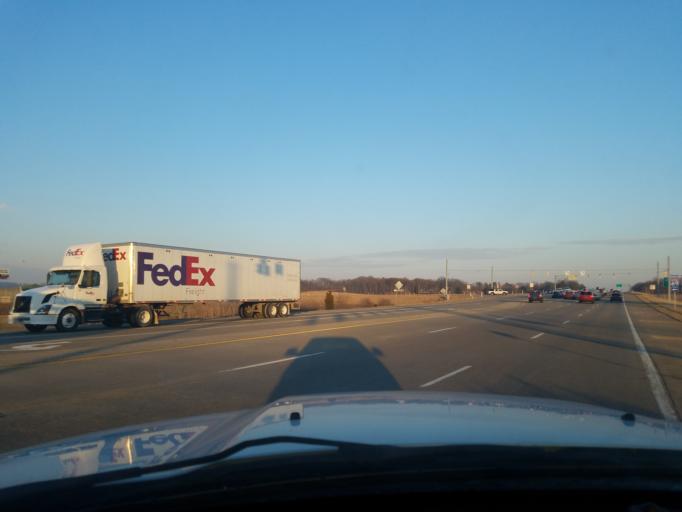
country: US
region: Indiana
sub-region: Vanderburgh County
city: Melody Hill
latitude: 38.0125
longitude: -87.4734
